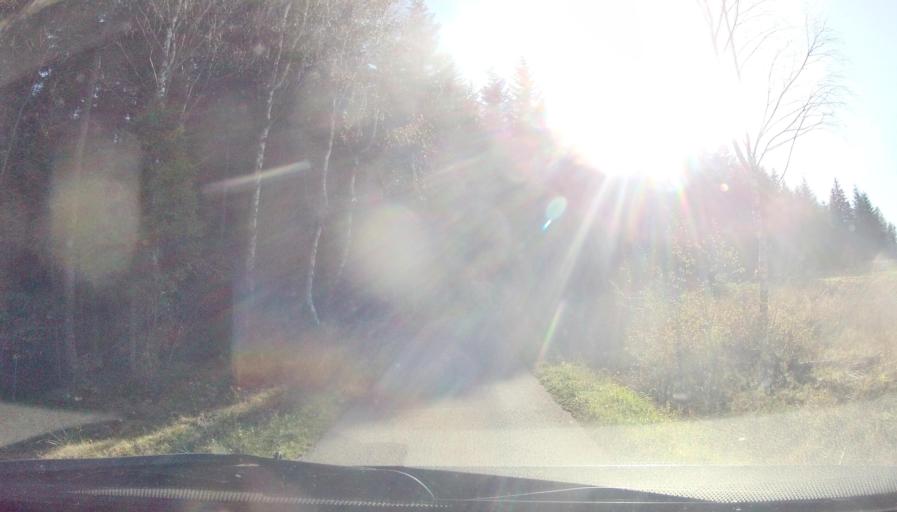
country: PL
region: Lesser Poland Voivodeship
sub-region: Powiat suski
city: Krzeszow
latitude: 49.7609
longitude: 19.4493
